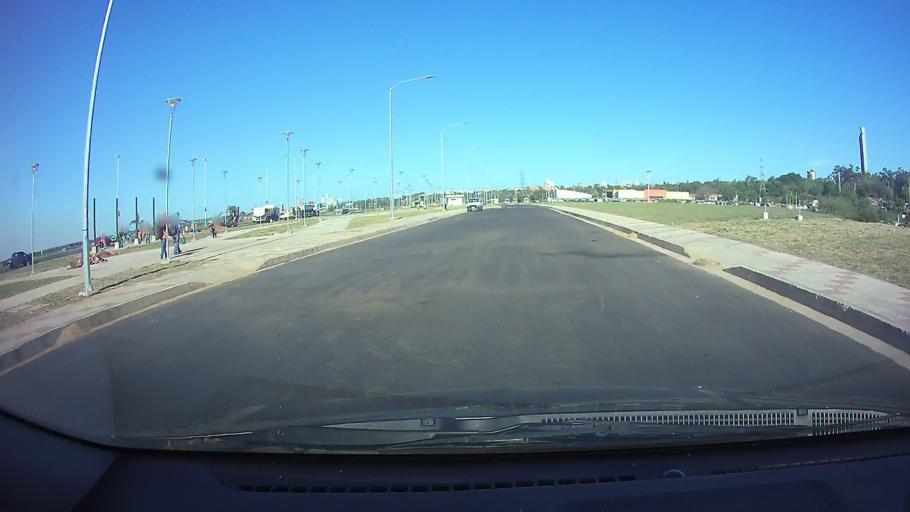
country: PY
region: Asuncion
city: Asuncion
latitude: -25.2770
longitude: -57.6256
